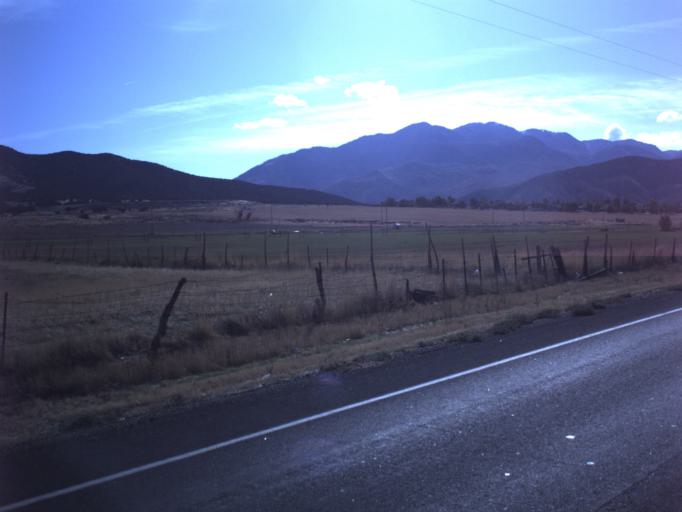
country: US
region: Utah
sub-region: Juab County
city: Nephi
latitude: 39.7377
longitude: -111.8371
